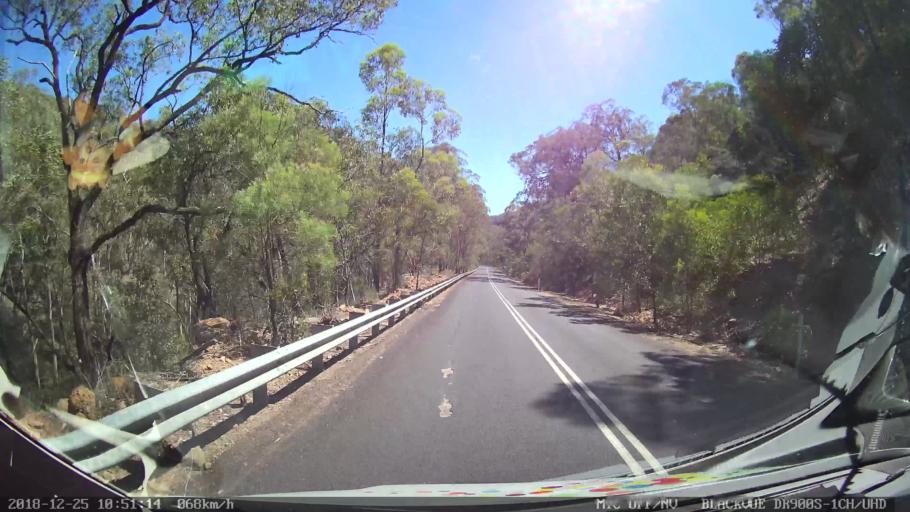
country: AU
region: New South Wales
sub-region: Upper Hunter Shire
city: Merriwa
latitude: -32.4388
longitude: 150.2685
